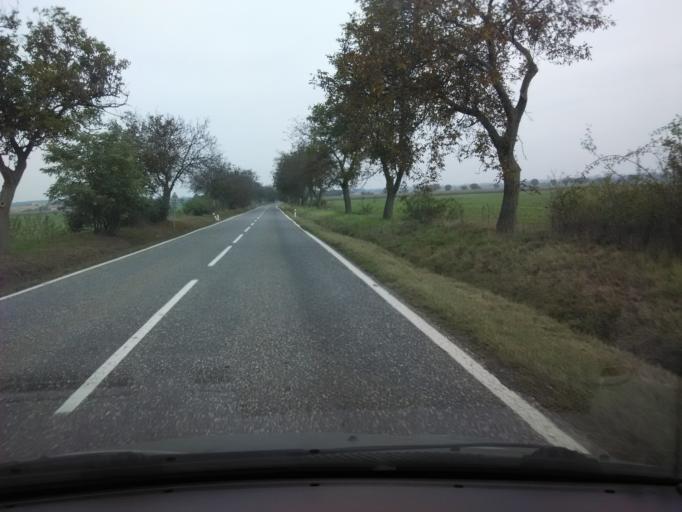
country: SK
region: Nitriansky
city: Svodin
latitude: 48.0541
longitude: 18.4934
